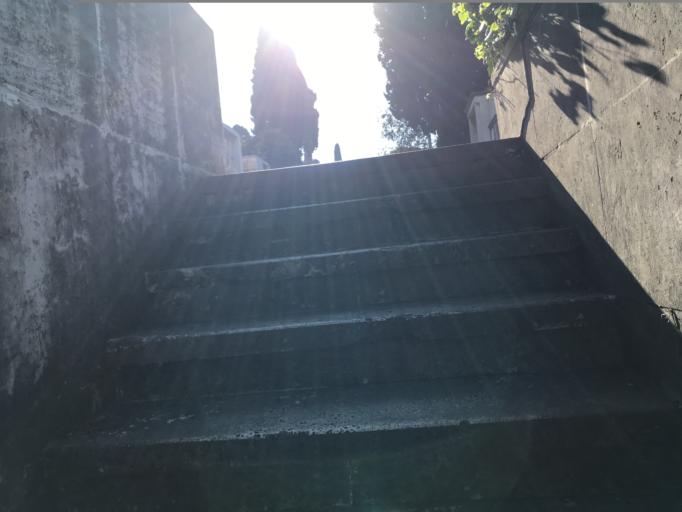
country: IT
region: Latium
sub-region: Citta metropolitana di Roma Capitale
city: Rome
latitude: 41.9012
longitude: 12.5209
